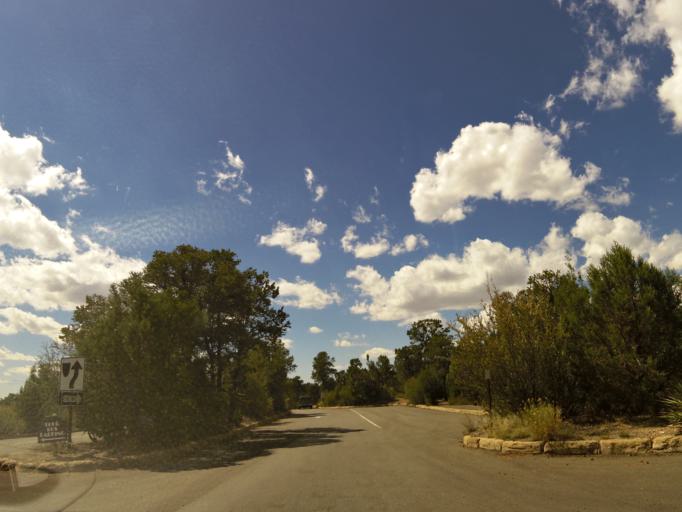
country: US
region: Colorado
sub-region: Montezuma County
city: Cortez
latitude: 37.1882
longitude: -108.4882
